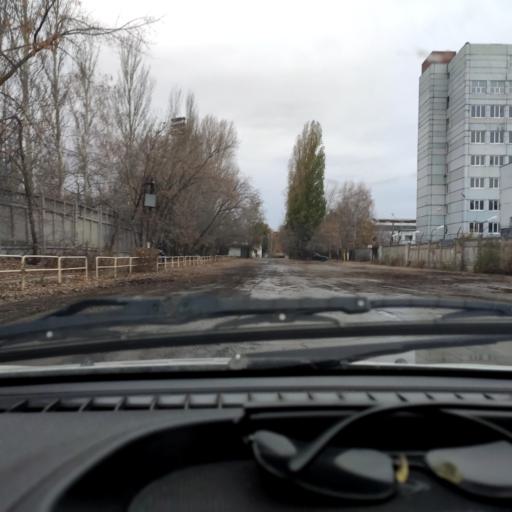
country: RU
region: Samara
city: Tol'yatti
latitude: 53.5176
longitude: 49.4594
